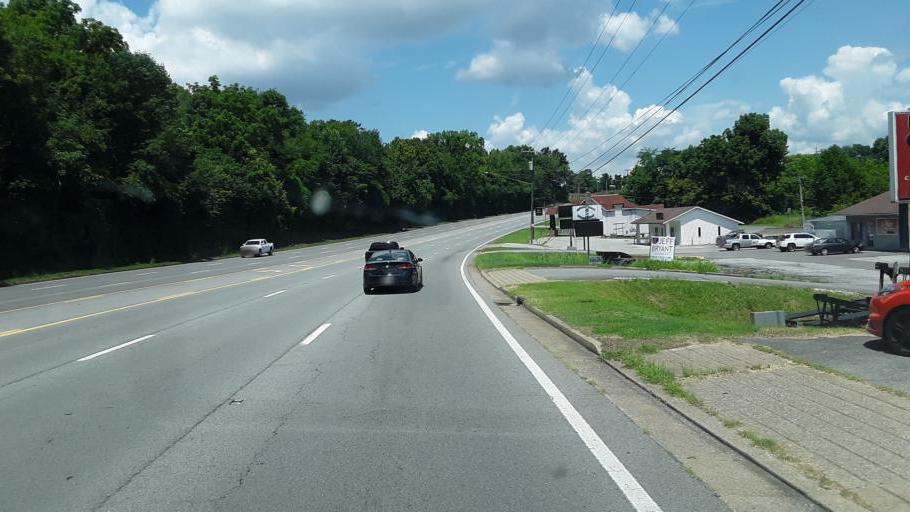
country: US
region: Kentucky
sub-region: Christian County
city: Fort Campbell North
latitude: 36.6113
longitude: -87.4295
